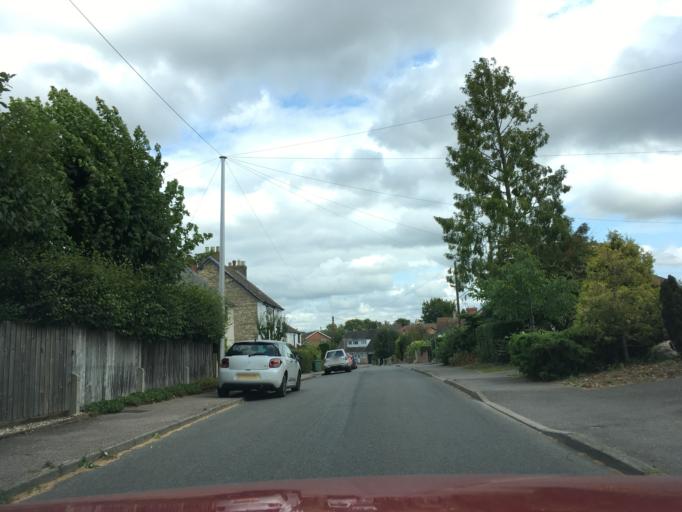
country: GB
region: England
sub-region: Kent
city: Maidstone
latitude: 51.2333
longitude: 0.5279
